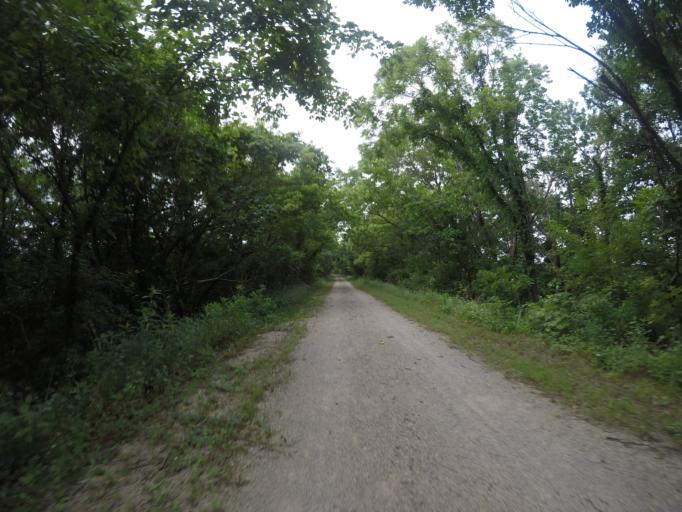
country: US
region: Kansas
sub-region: Franklin County
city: Ottawa
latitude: 38.4816
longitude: -95.2750
